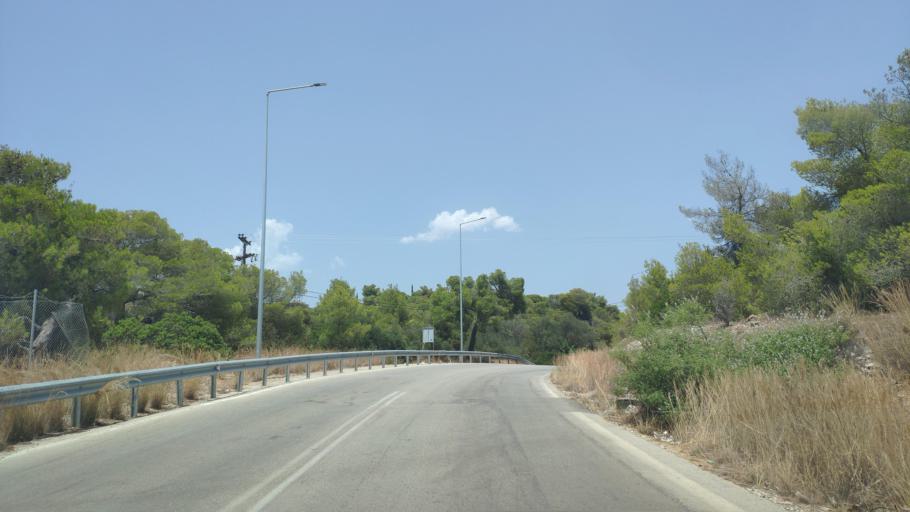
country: GR
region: Peloponnese
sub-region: Nomos Argolidos
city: Porto Cheli
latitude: 37.3350
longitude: 23.1524
